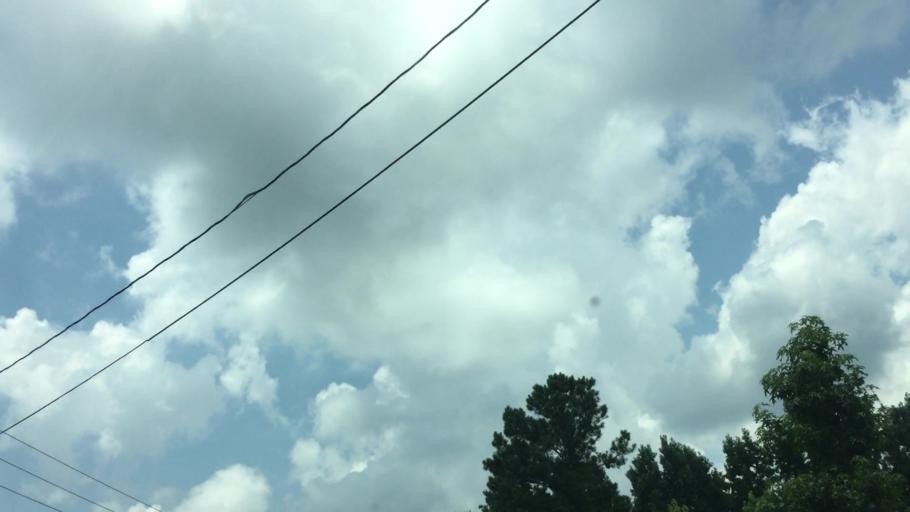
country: US
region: Georgia
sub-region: Carroll County
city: Villa Rica
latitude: 33.6124
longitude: -84.9340
